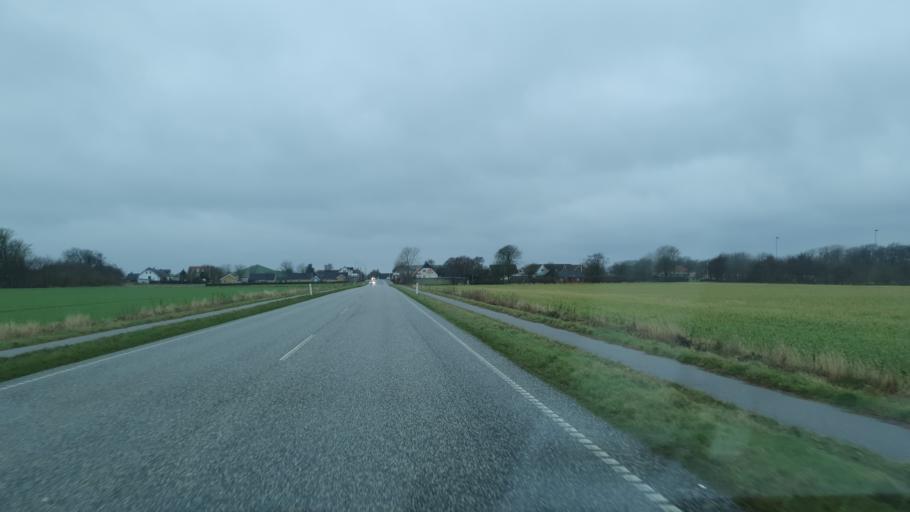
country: DK
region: North Denmark
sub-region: Jammerbugt Kommune
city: Fjerritslev
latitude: 57.1021
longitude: 9.1325
